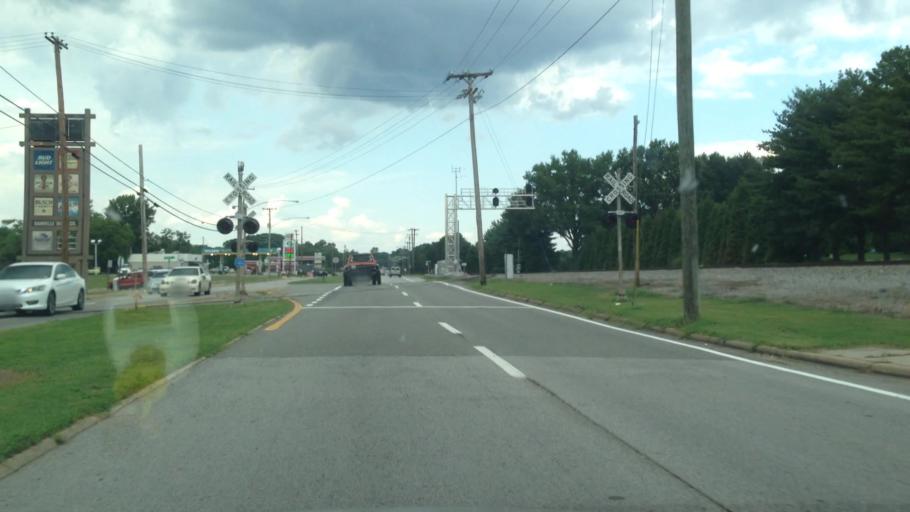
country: US
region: Virginia
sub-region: City of Danville
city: Danville
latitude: 36.5504
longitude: -79.4604
